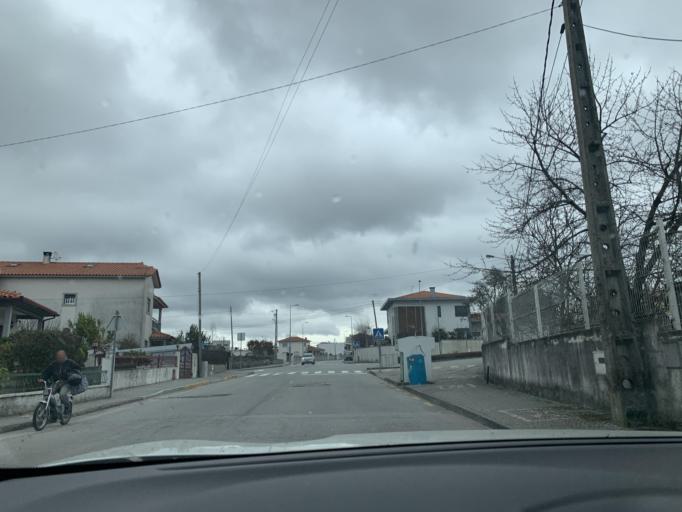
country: PT
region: Viseu
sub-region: Mangualde
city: Mangualde
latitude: 40.6119
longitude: -7.7663
